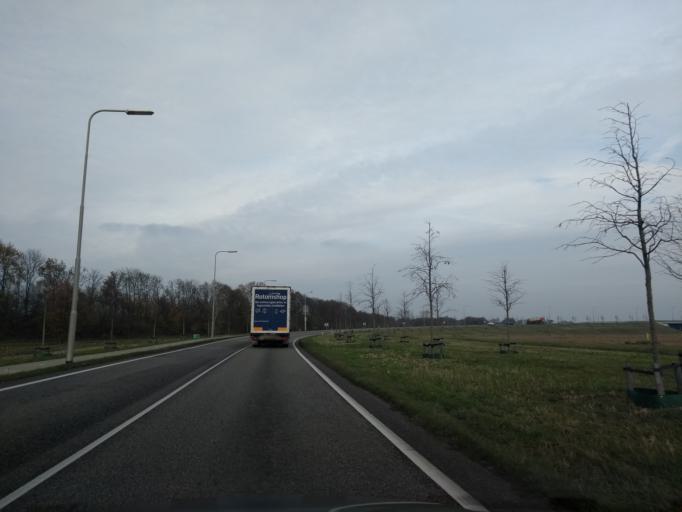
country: NL
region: Limburg
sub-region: Gemeente Sittard-Geleen
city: Born
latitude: 51.0705
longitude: 5.8198
